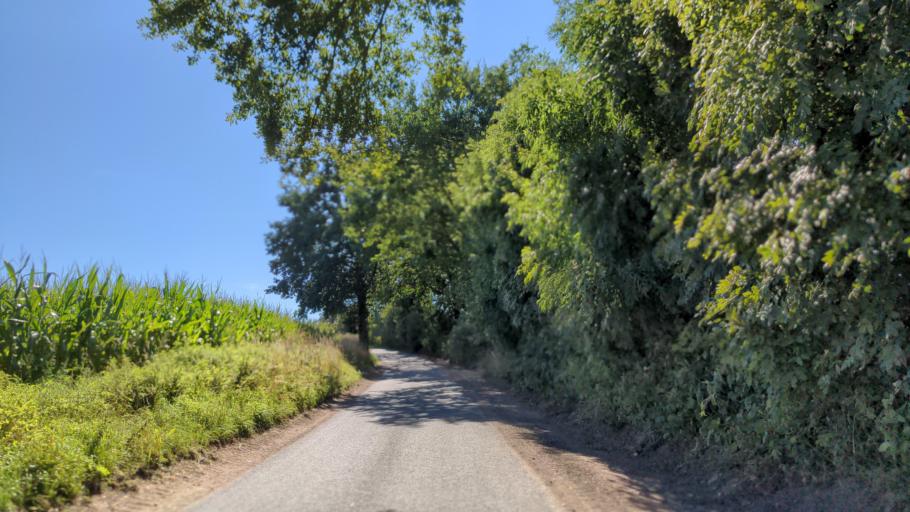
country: DE
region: Schleswig-Holstein
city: Kasseedorf
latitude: 54.1254
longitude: 10.7155
